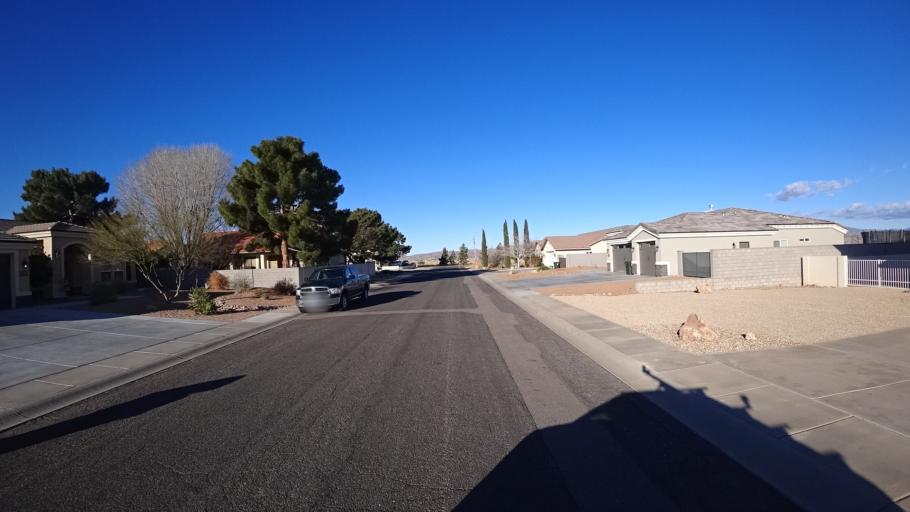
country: US
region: Arizona
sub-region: Mohave County
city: New Kingman-Butler
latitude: 35.2240
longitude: -113.9747
